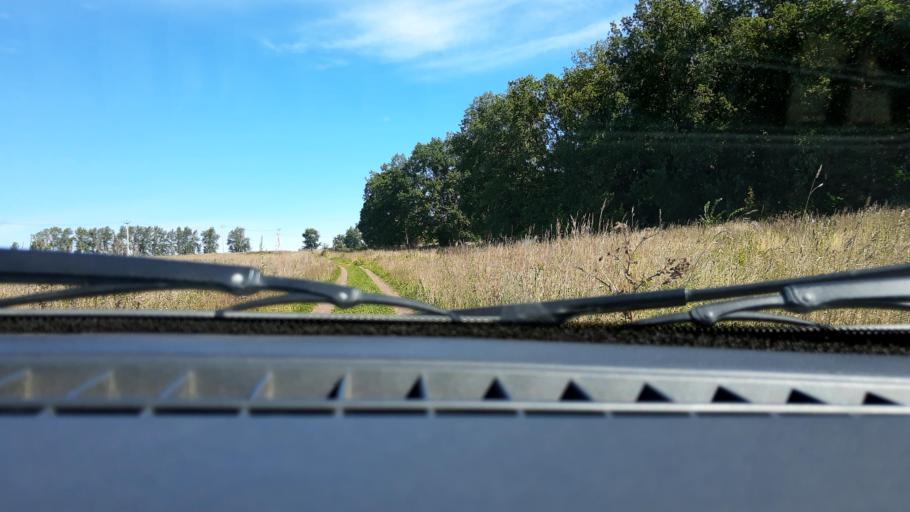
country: RU
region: Bashkortostan
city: Mikhaylovka
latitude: 54.8235
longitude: 55.7945
